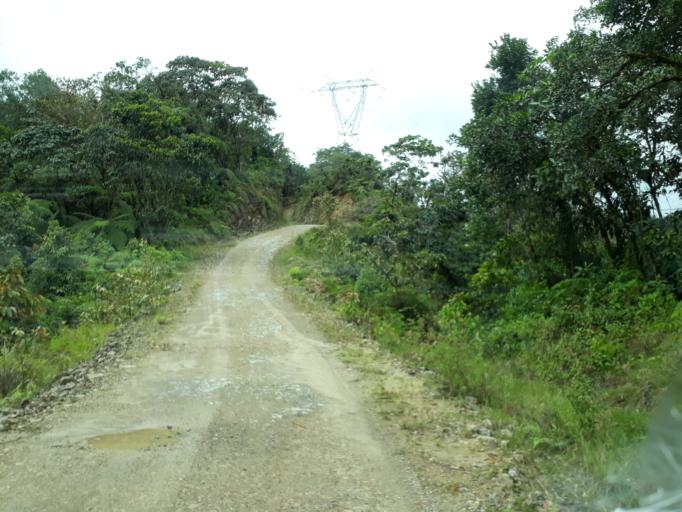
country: CO
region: Cundinamarca
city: Gachala
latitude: 4.7109
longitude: -73.3905
